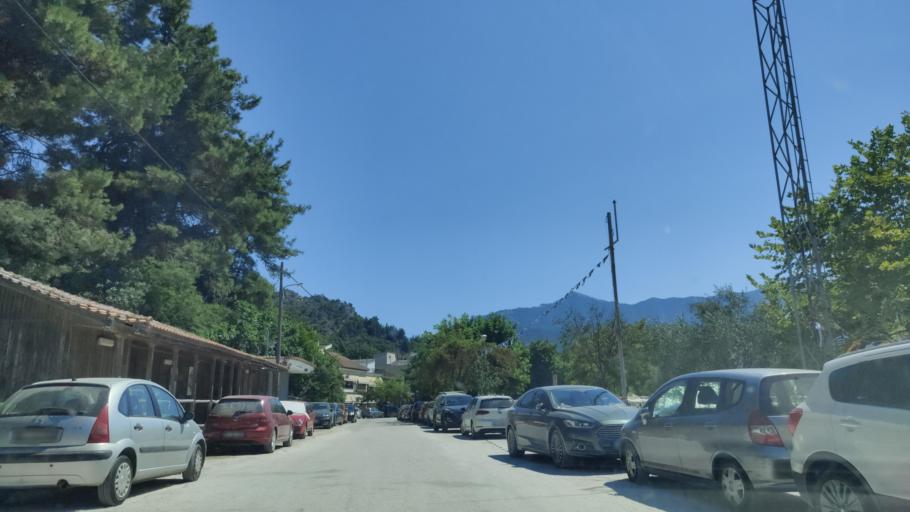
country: GR
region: East Macedonia and Thrace
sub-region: Nomos Kavalas
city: Thasos
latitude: 40.7842
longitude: 24.7153
